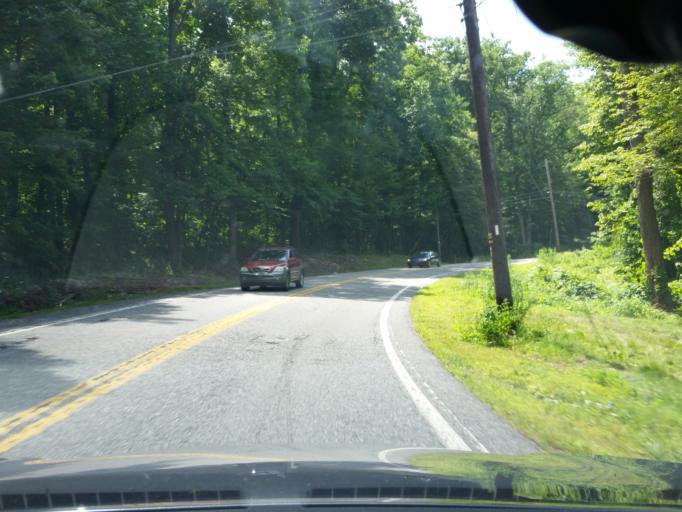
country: US
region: Pennsylvania
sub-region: Dauphin County
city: Matamoras
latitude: 40.4121
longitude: -76.9441
